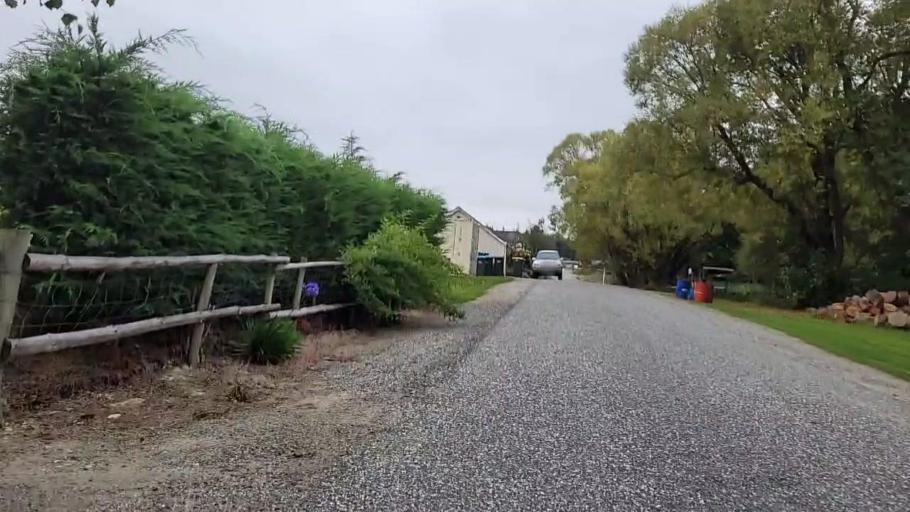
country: NZ
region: Otago
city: Oamaru
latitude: -45.0241
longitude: 170.1482
